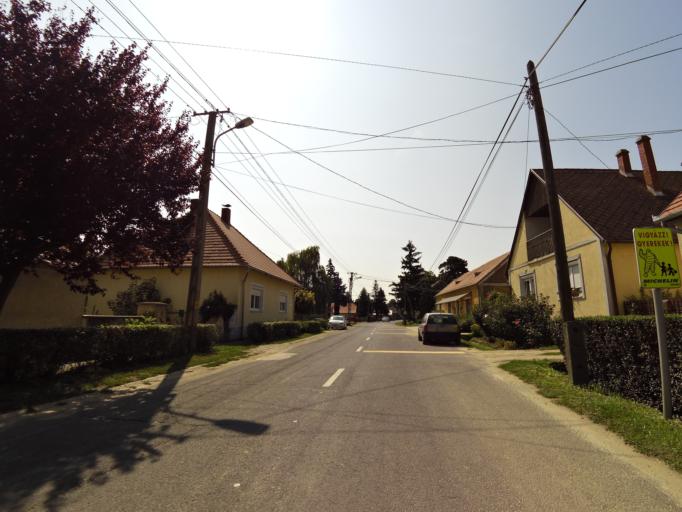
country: HU
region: Zala
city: Vonyarcvashegy
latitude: 46.8089
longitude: 17.3814
